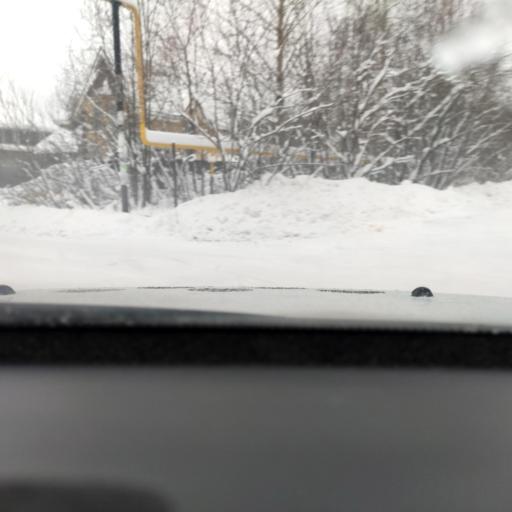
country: RU
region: Perm
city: Polazna
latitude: 58.1425
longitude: 56.4326
